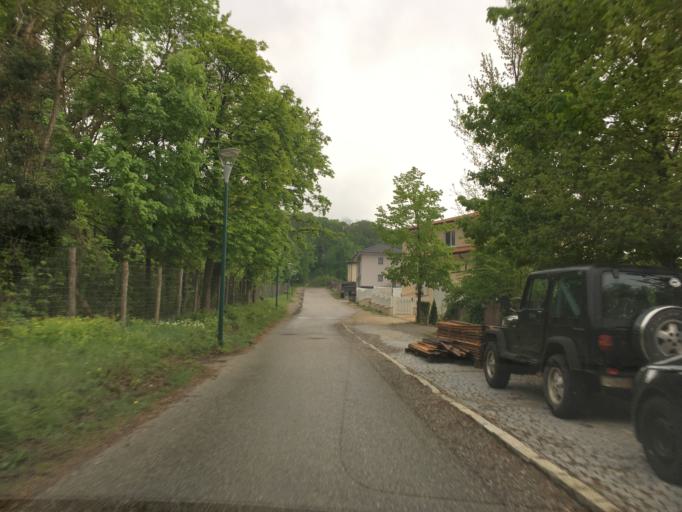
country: AT
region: Burgenland
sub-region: Politischer Bezirk Neusiedl am See
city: Bruckneudorf
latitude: 48.0154
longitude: 16.7791
